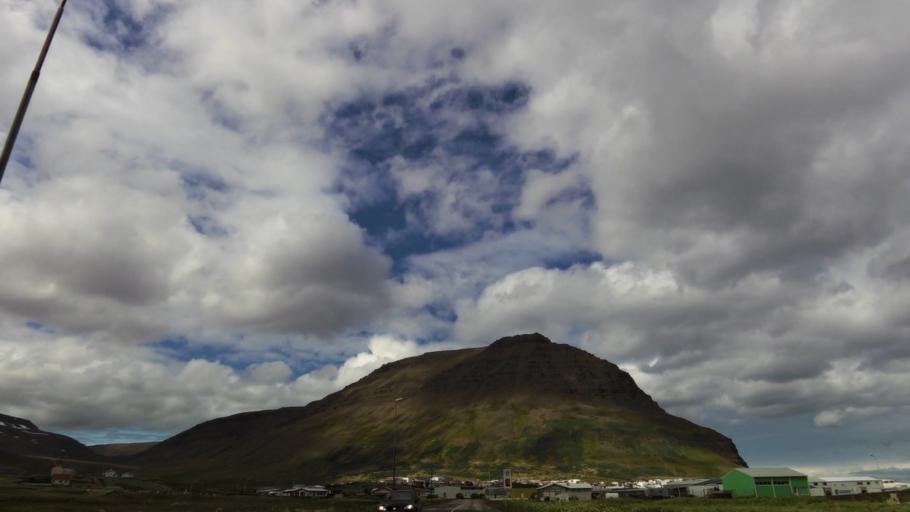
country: IS
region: Westfjords
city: Isafjoerdur
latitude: 66.1518
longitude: -23.2474
